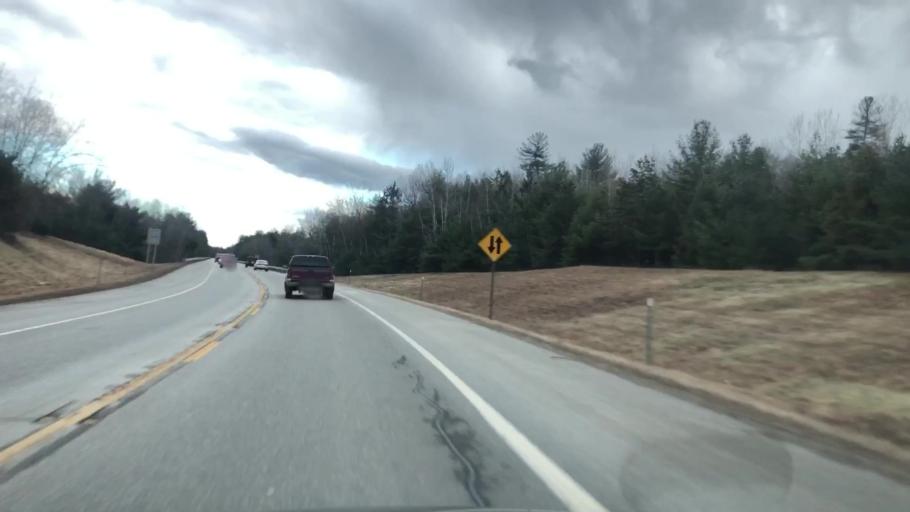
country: US
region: New Hampshire
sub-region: Hillsborough County
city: Wilton
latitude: 42.8358
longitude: -71.6992
